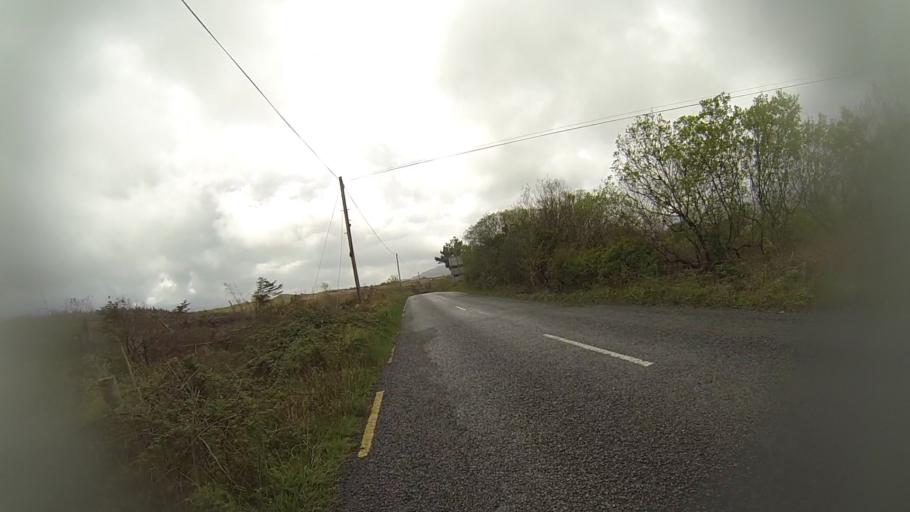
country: IE
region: Munster
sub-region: Ciarrai
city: Killorglin
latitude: 51.8521
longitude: -9.8793
